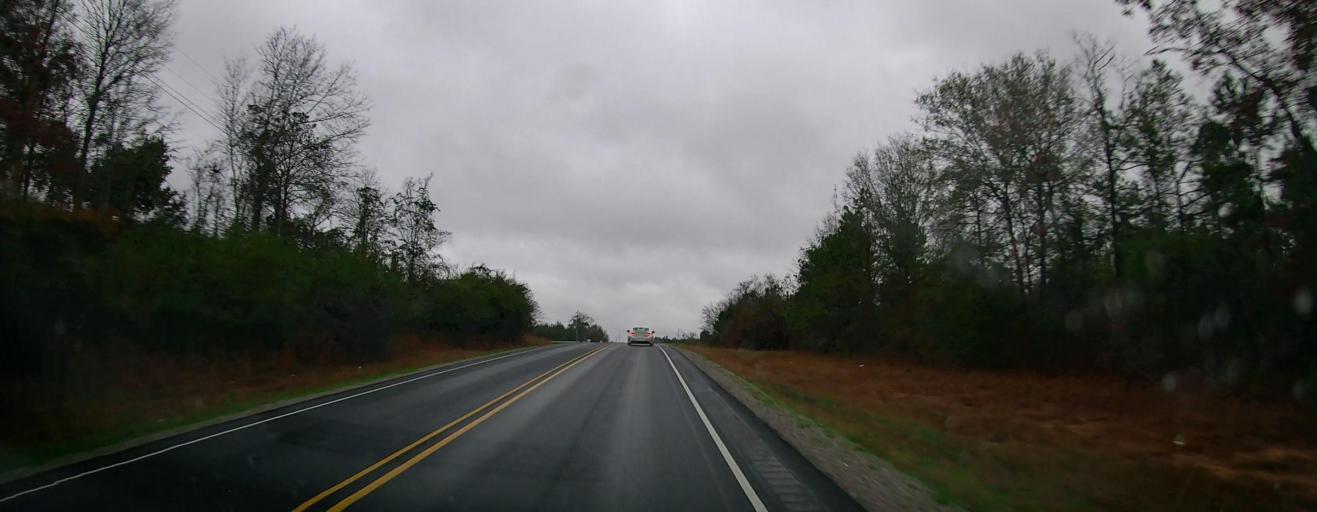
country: US
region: Alabama
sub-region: Chilton County
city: Clanton
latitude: 32.6503
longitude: -86.7654
